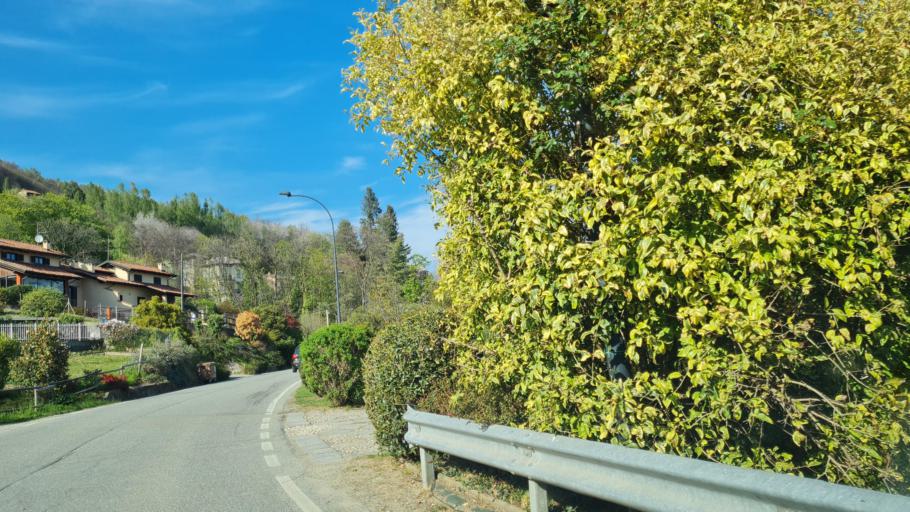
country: IT
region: Piedmont
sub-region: Provincia di Biella
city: Sordevolo
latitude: 45.5779
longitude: 7.9826
